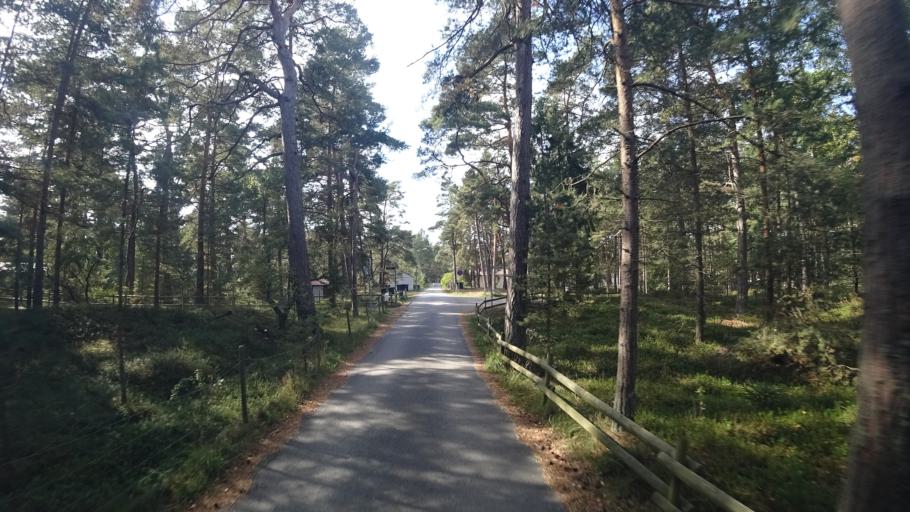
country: SE
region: Skane
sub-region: Kristianstads Kommun
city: Ahus
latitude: 55.9138
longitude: 14.3087
